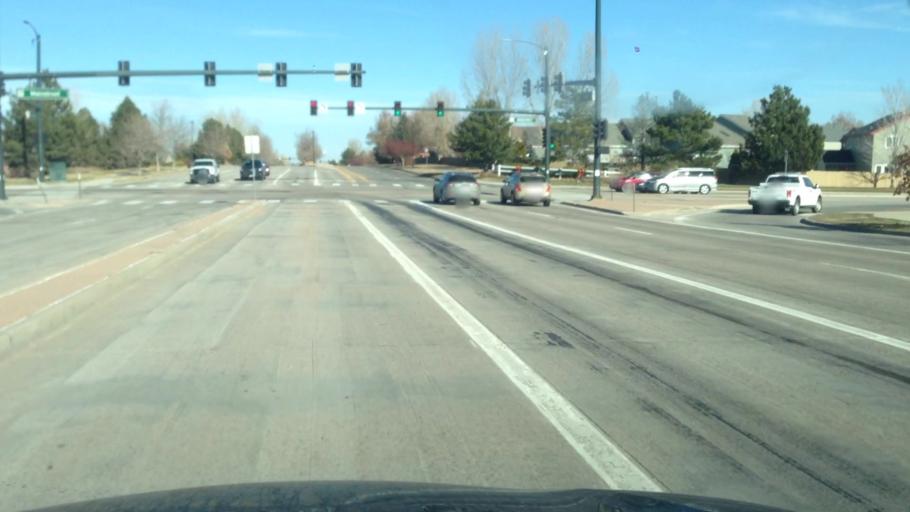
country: US
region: Colorado
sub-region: Douglas County
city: Stonegate
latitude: 39.5143
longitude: -104.7934
